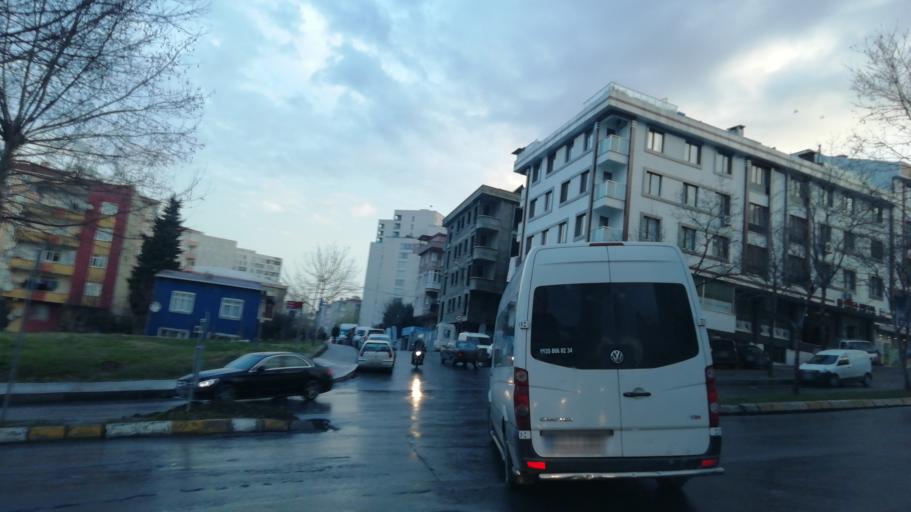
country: TR
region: Istanbul
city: Mahmutbey
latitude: 41.0220
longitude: 28.8243
